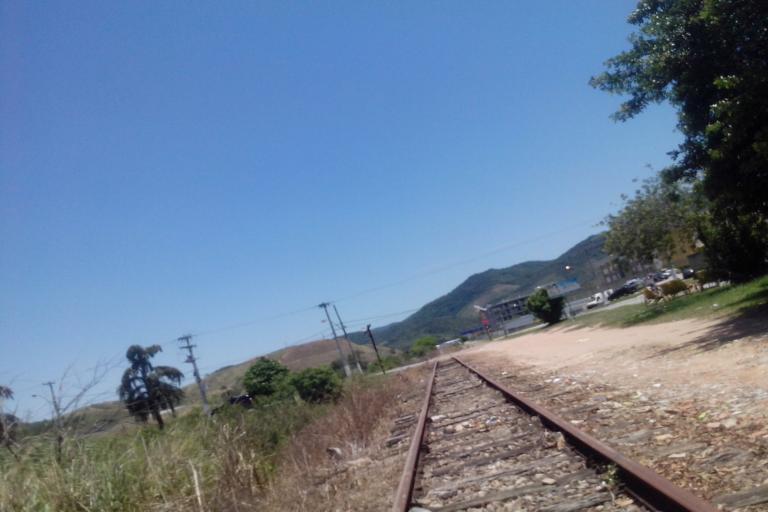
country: BR
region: Rio de Janeiro
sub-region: Rio Bonito
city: Rio Bonito
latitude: -22.7081
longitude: -42.6473
